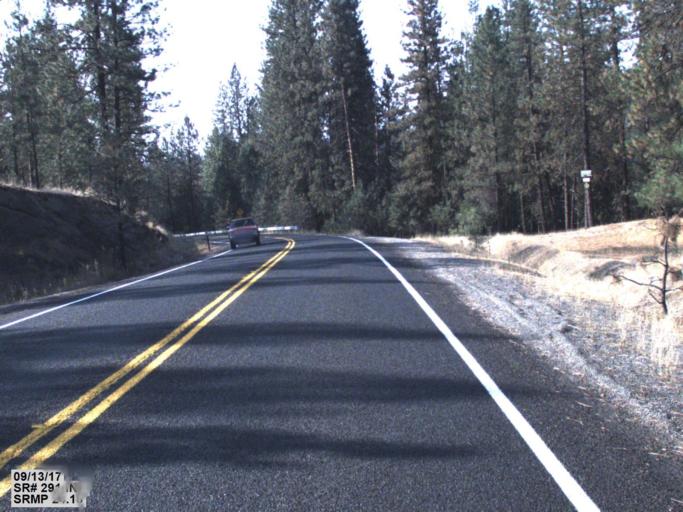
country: US
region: Washington
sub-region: Spokane County
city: Deer Park
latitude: 47.8770
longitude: -117.7080
